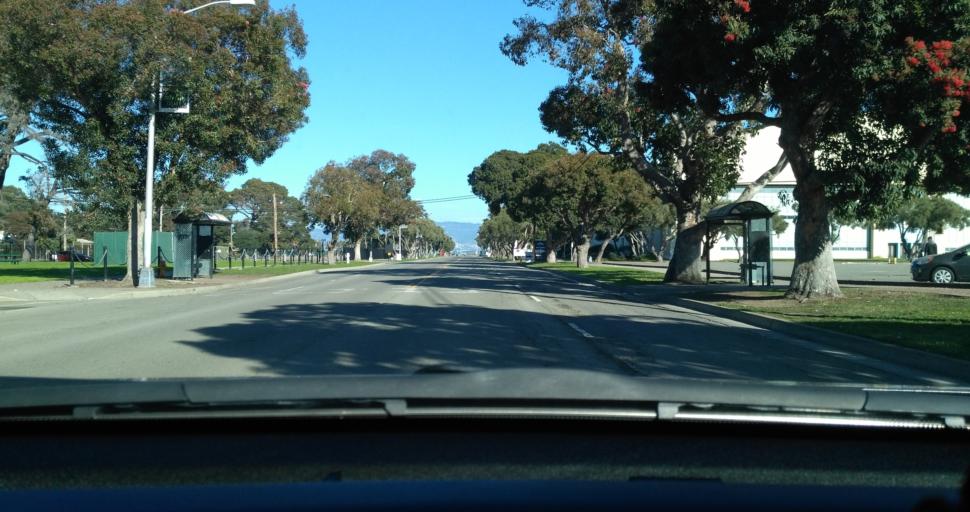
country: US
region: California
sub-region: San Francisco County
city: San Francisco
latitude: 37.8184
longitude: -122.3700
